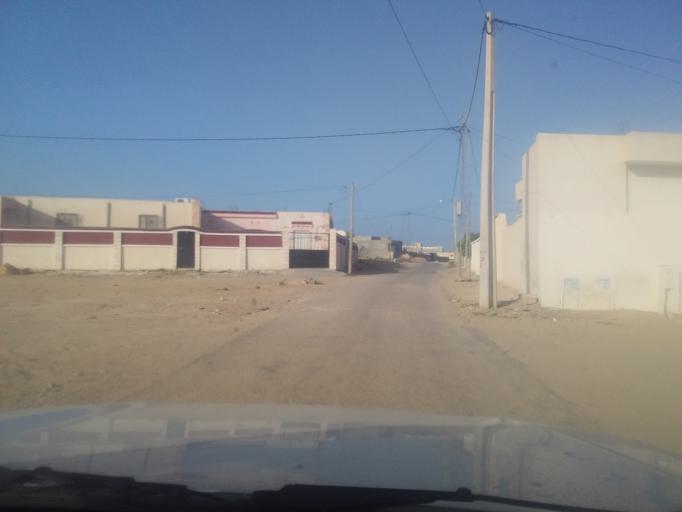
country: TN
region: Qabis
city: Gabes
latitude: 33.6348
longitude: 10.2874
